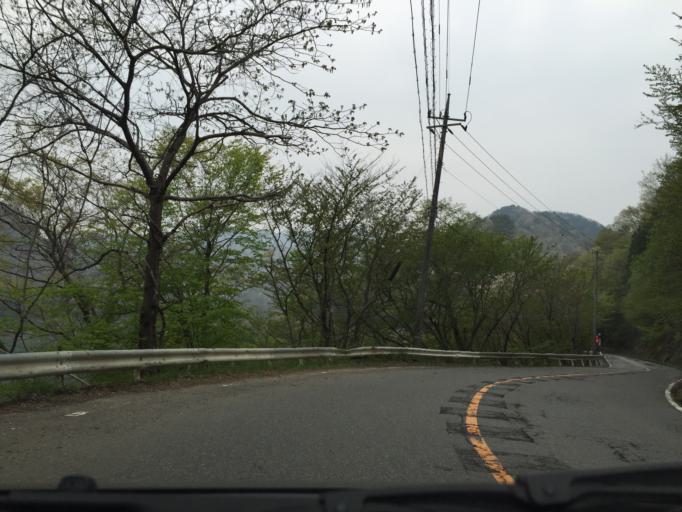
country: JP
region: Tochigi
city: Nikko
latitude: 36.9424
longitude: 139.6983
